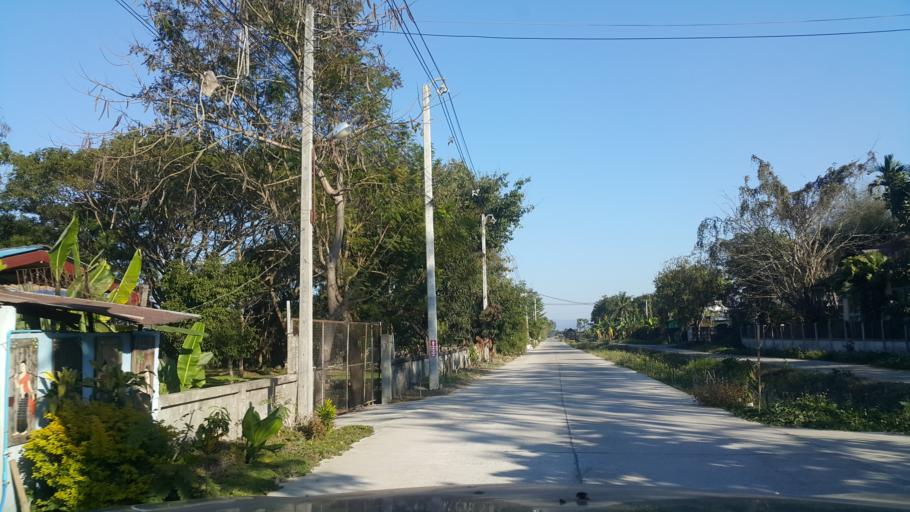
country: TH
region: Chiang Mai
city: Hang Dong
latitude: 18.6786
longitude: 98.9559
